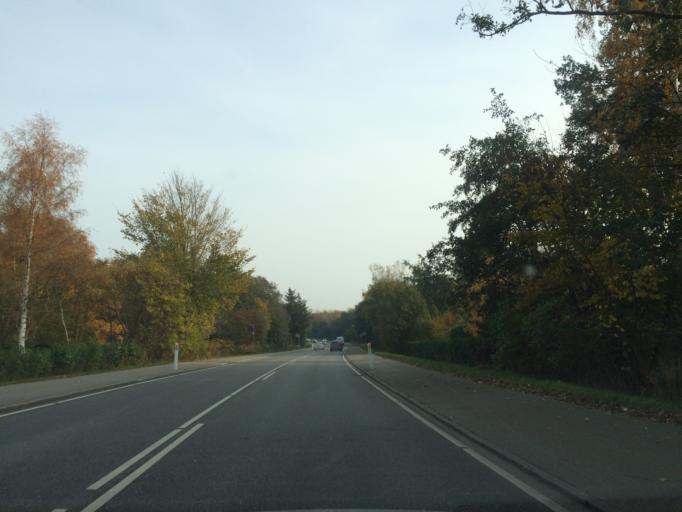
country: DK
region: Zealand
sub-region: Odsherred Kommune
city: Asnaes
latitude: 55.9794
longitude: 11.3221
